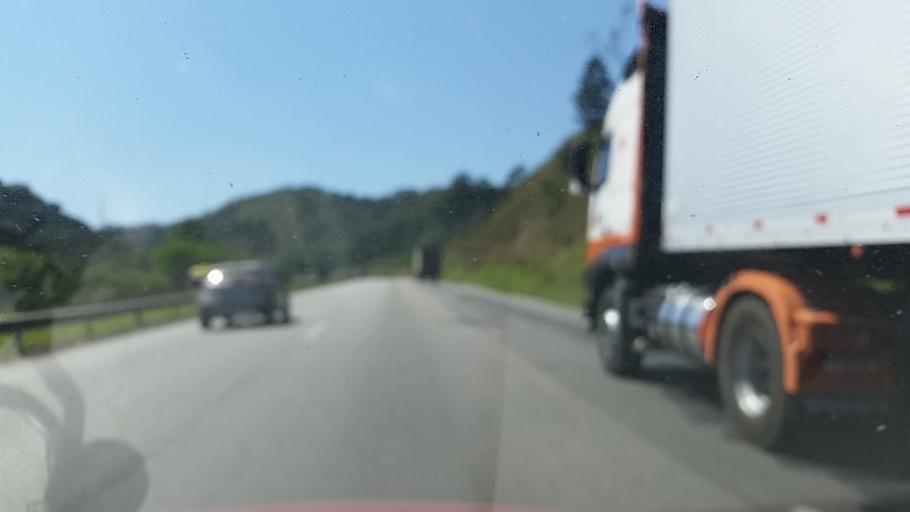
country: BR
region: Sao Paulo
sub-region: Juquitiba
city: Juquitiba
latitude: -23.9976
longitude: -47.1490
